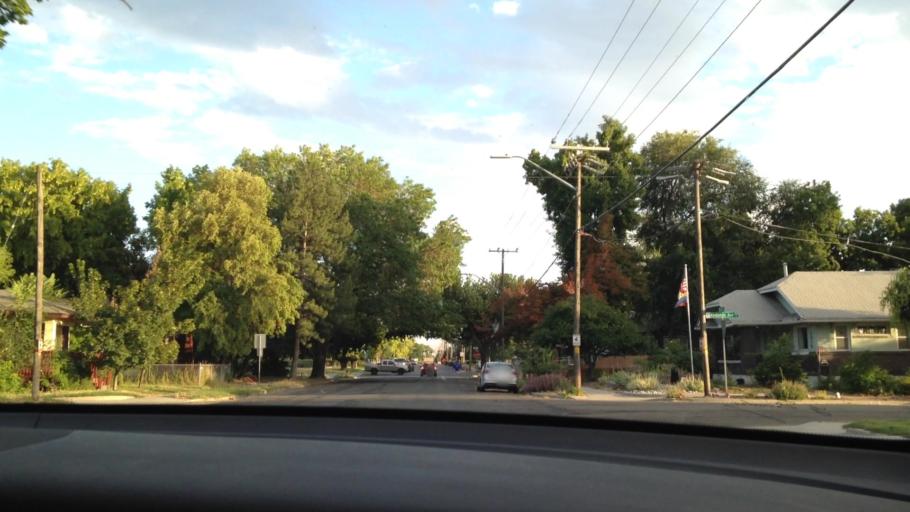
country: US
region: Utah
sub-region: Salt Lake County
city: South Salt Lake
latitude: 40.7266
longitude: -111.8797
